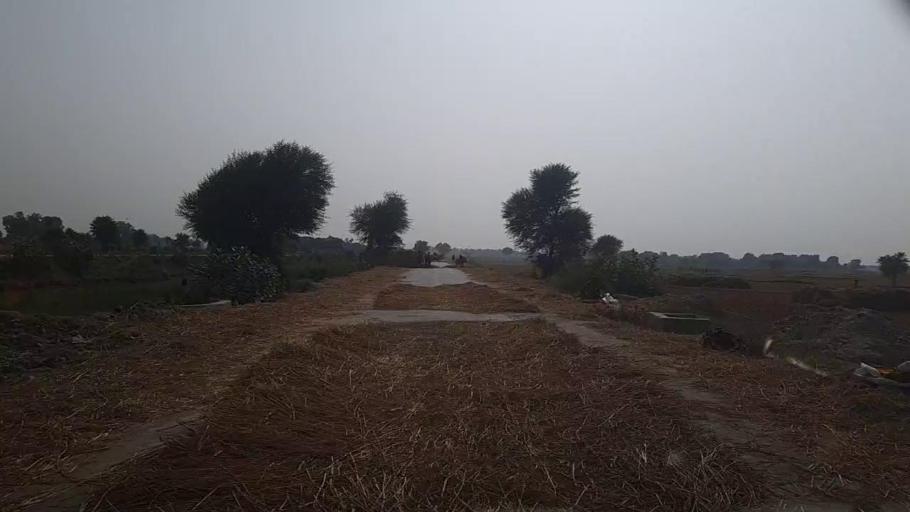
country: PK
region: Sindh
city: Kashmor
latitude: 28.4185
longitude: 69.5695
